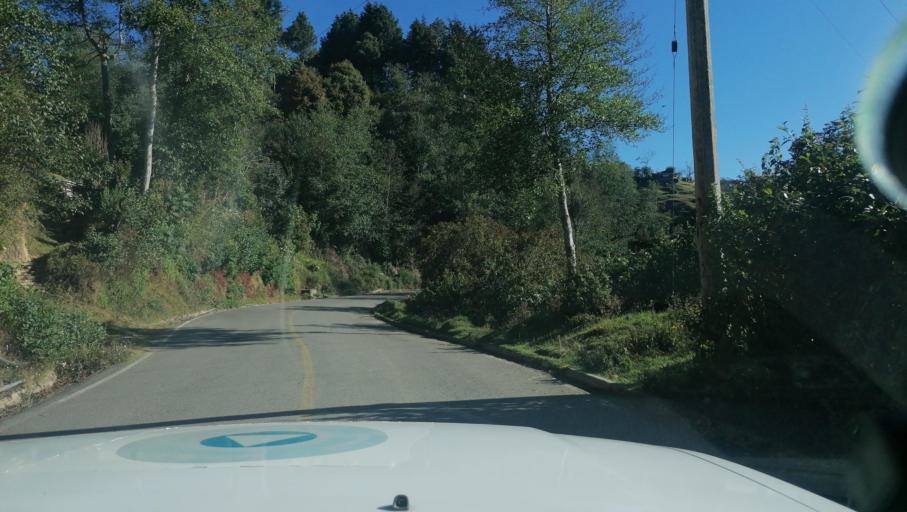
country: MX
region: Chiapas
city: Motozintla de Mendoza
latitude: 15.2507
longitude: -92.2238
